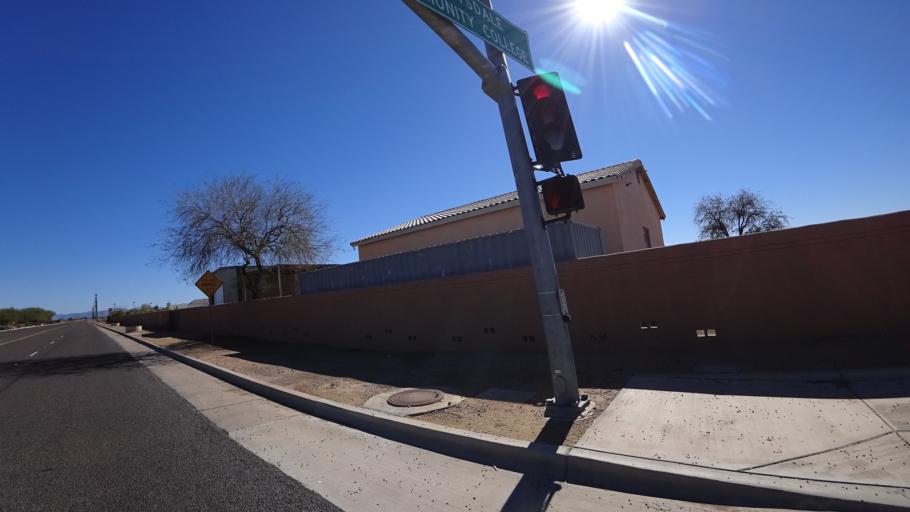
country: US
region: Arizona
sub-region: Maricopa County
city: Scottsdale
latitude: 33.5094
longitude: -111.8826
